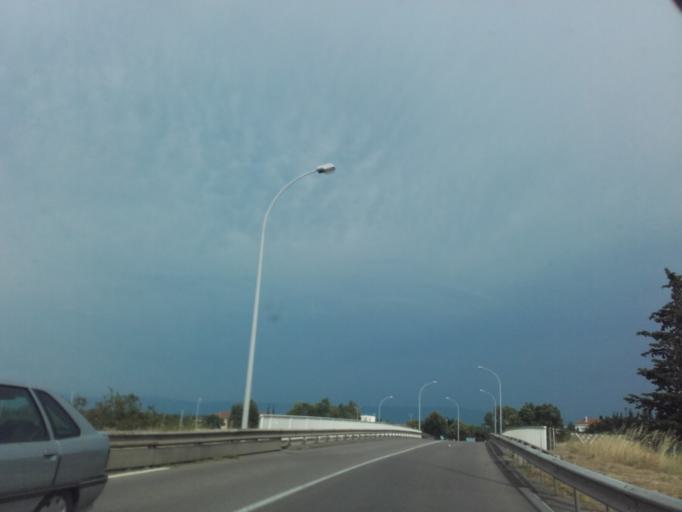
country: FR
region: Rhone-Alpes
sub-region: Departement de la Drome
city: Portes-les-Valence
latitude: 44.8715
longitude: 4.8643
